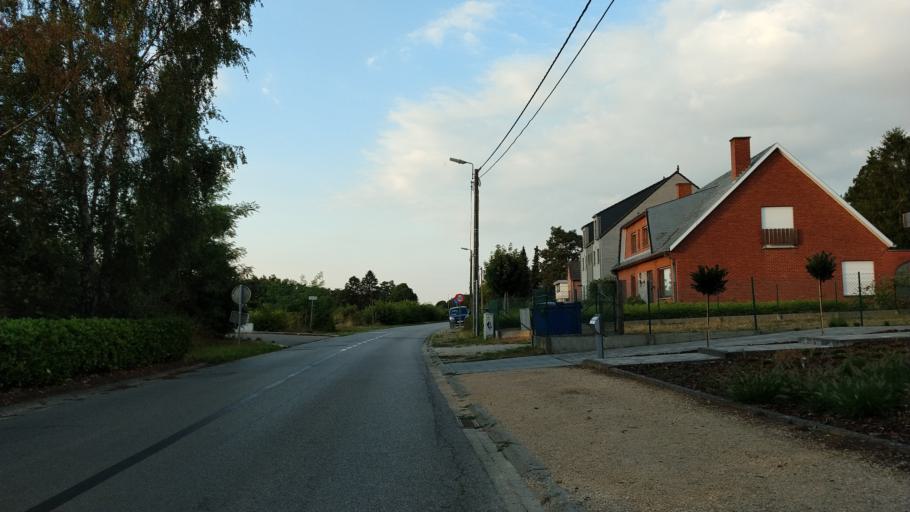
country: BE
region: Flanders
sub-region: Provincie Vlaams-Brabant
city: Oud-Heverlee
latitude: 50.8448
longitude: 4.6661
